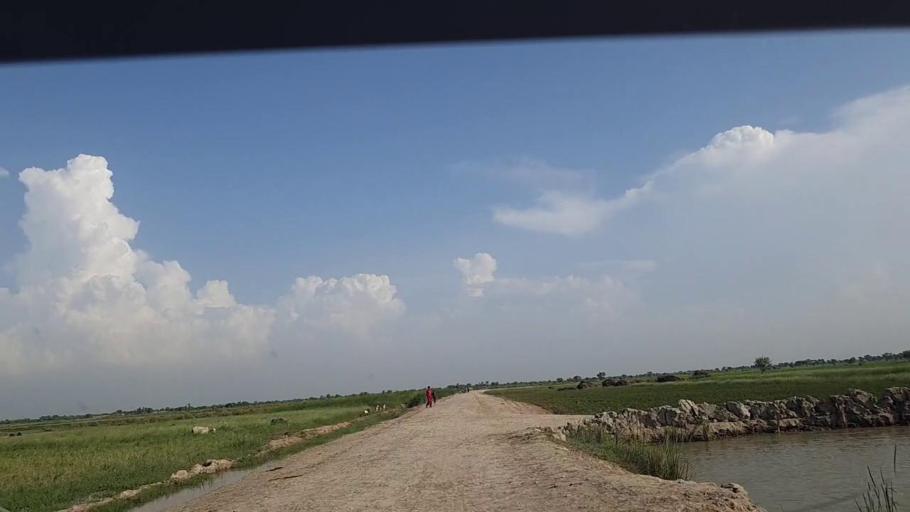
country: PK
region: Sindh
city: Khanpur
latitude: 27.8581
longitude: 69.3762
